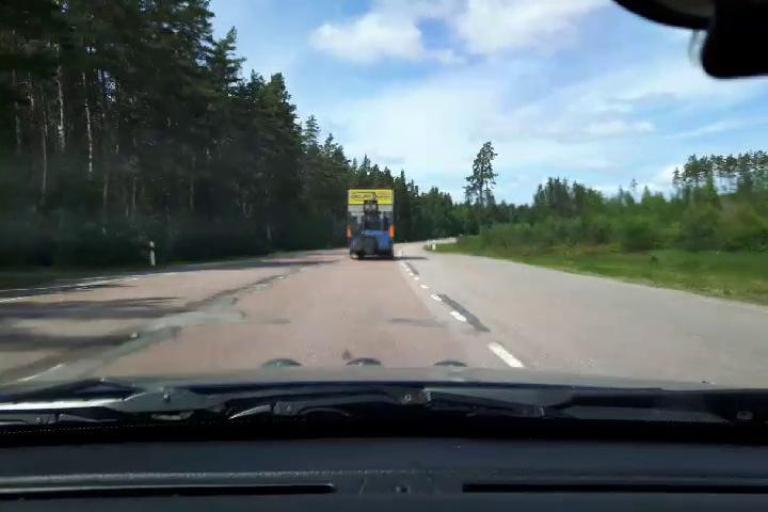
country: SE
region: Uppsala
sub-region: Osthammars Kommun
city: Bjorklinge
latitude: 60.1206
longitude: 17.5116
